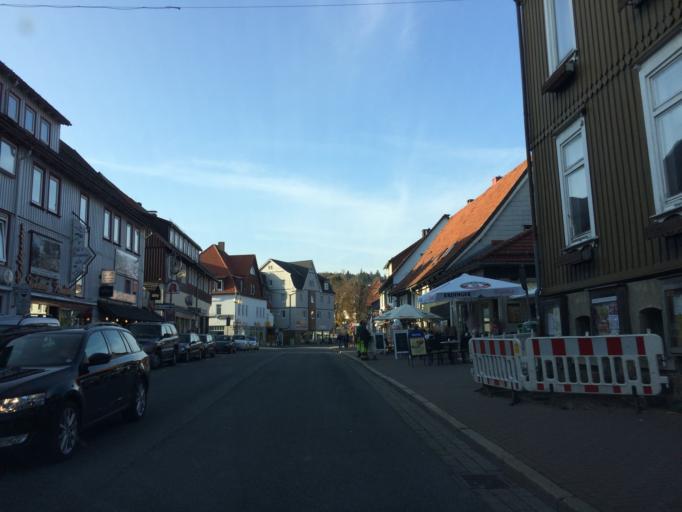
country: DE
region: Lower Saxony
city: Braunlage
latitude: 51.7255
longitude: 10.6109
